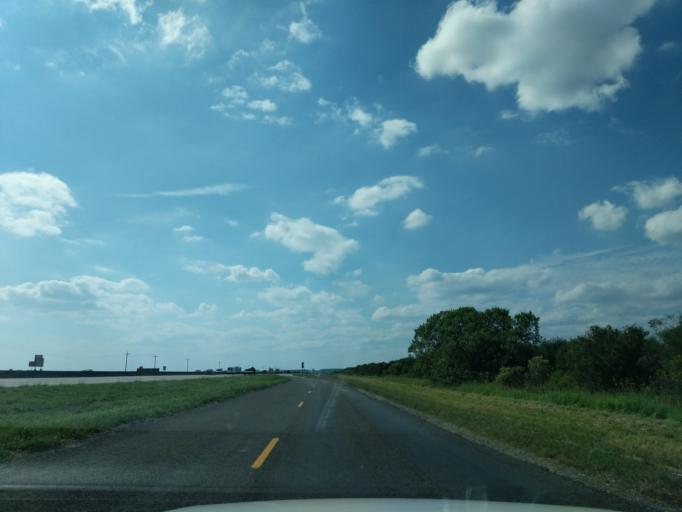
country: US
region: Texas
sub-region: Chambers County
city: Anahuac
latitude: 29.8352
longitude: -94.5435
